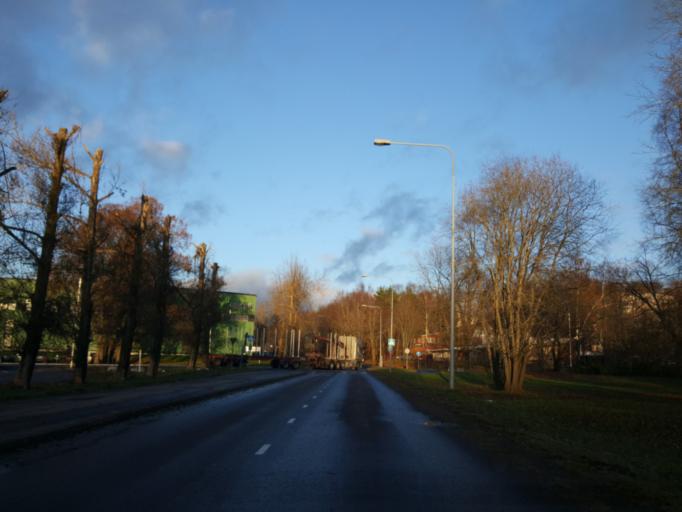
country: FI
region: Uusimaa
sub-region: Helsinki
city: Lohja
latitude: 60.2520
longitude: 24.0559
